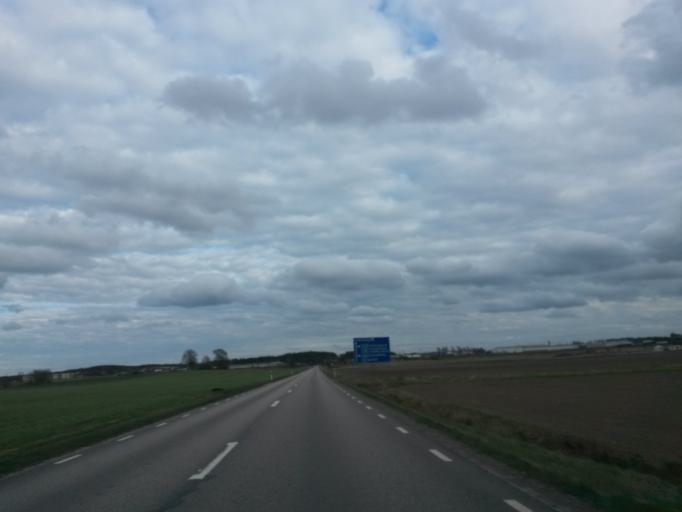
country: SE
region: Vaestra Goetaland
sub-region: Vargarda Kommun
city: Vargarda
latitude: 58.0466
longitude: 12.7868
